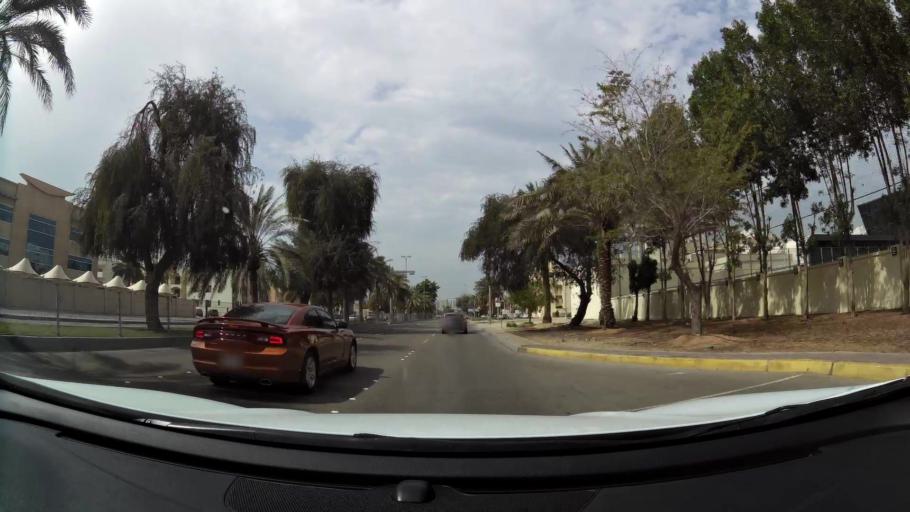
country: AE
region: Abu Dhabi
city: Abu Dhabi
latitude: 24.4571
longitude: 54.3603
